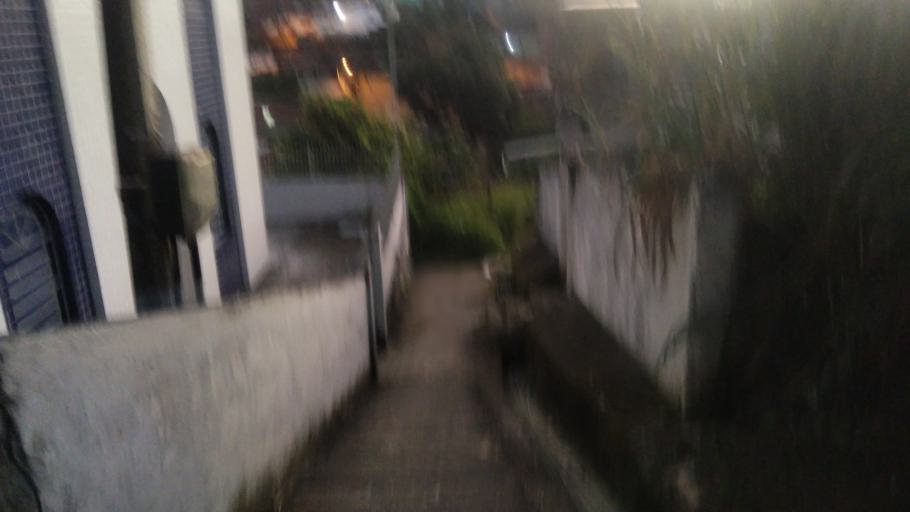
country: BR
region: Pernambuco
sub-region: Jaboatao Dos Guararapes
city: Jaboatao dos Guararapes
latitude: -8.0683
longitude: -35.0002
